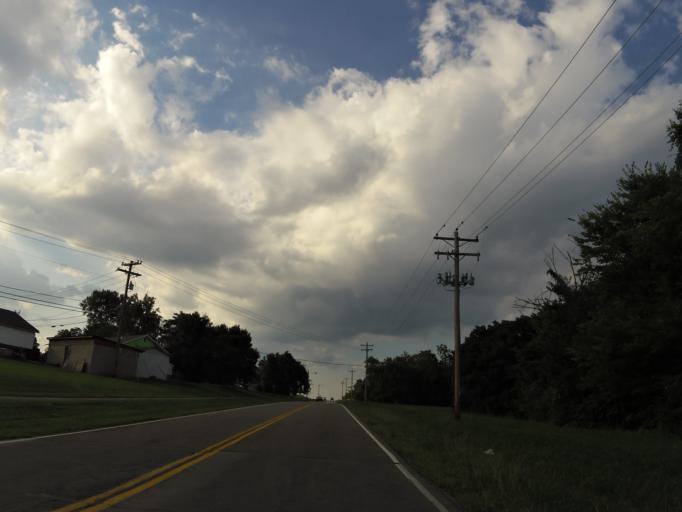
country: US
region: Tennessee
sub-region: Blount County
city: Alcoa
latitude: 35.7751
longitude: -83.9771
